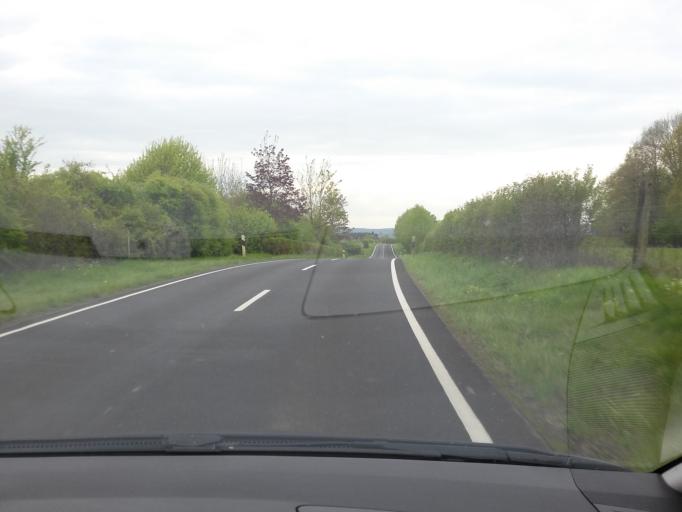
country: LU
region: Luxembourg
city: Hautcharage
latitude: 49.5880
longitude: 5.9113
